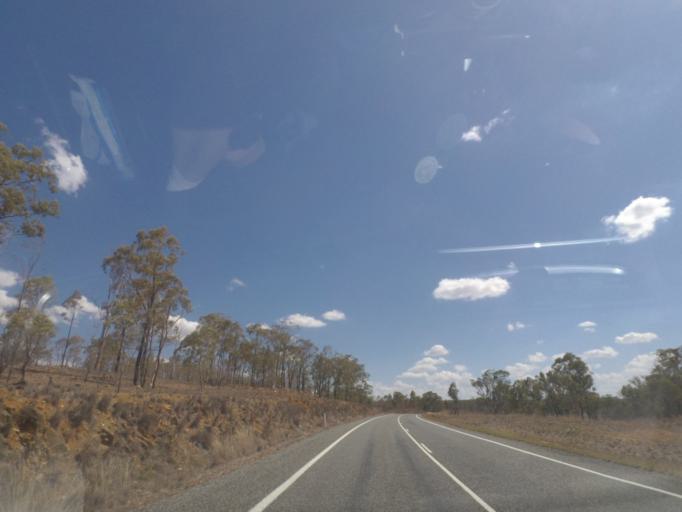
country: AU
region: Queensland
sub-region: Southern Downs
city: Warwick
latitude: -28.2136
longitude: 151.5638
